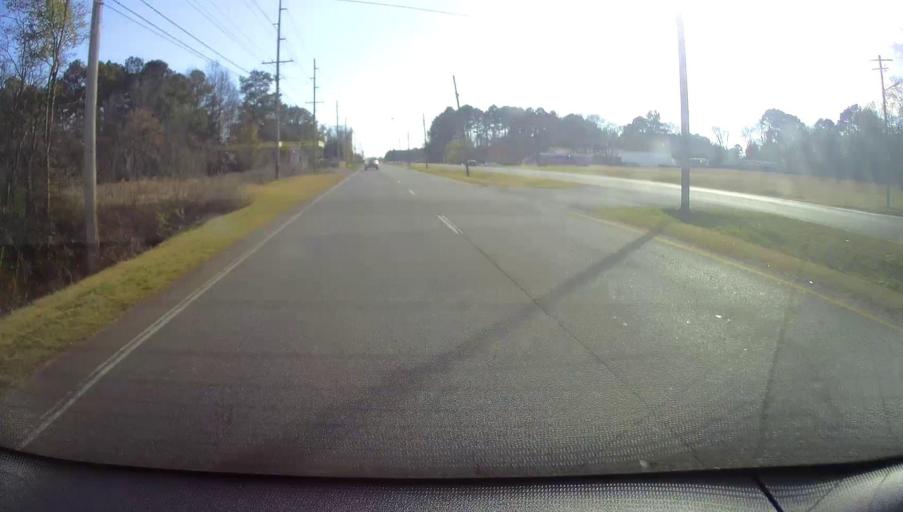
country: US
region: Alabama
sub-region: Limestone County
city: Athens
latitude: 34.7799
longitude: -86.9568
